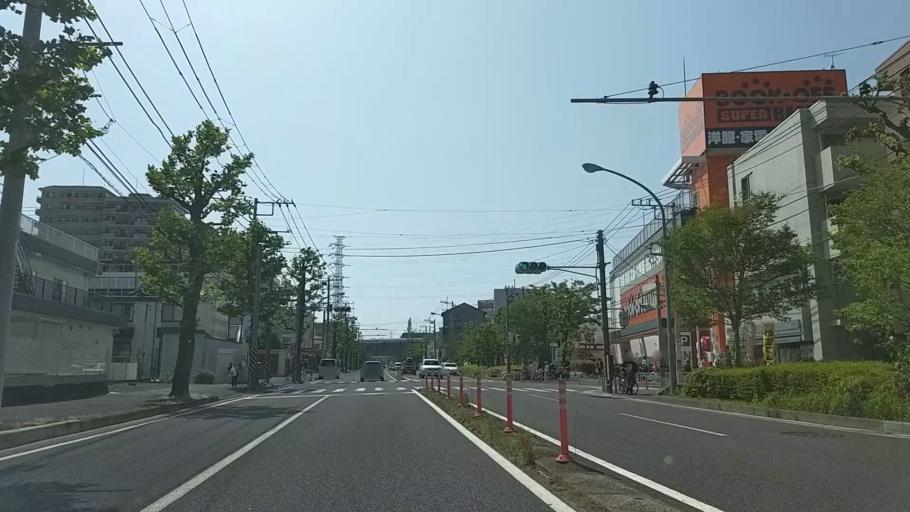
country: JP
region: Kanagawa
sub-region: Kawasaki-shi
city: Kawasaki
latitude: 35.5314
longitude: 139.6425
